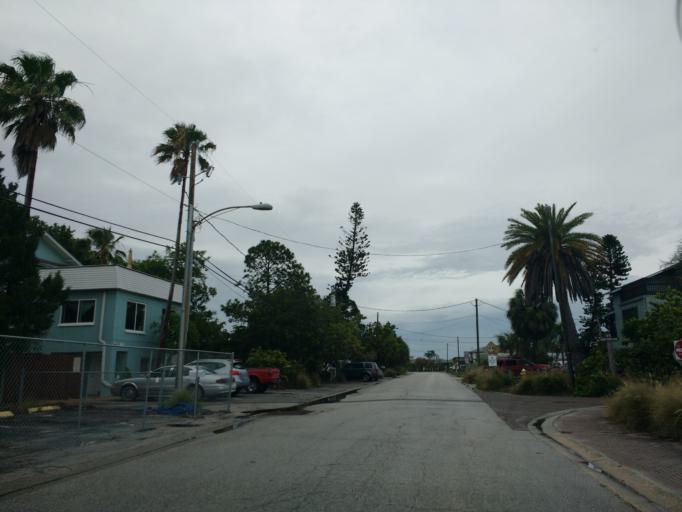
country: US
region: Florida
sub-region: Pinellas County
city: Madeira Beach
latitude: 27.7865
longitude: -82.7815
